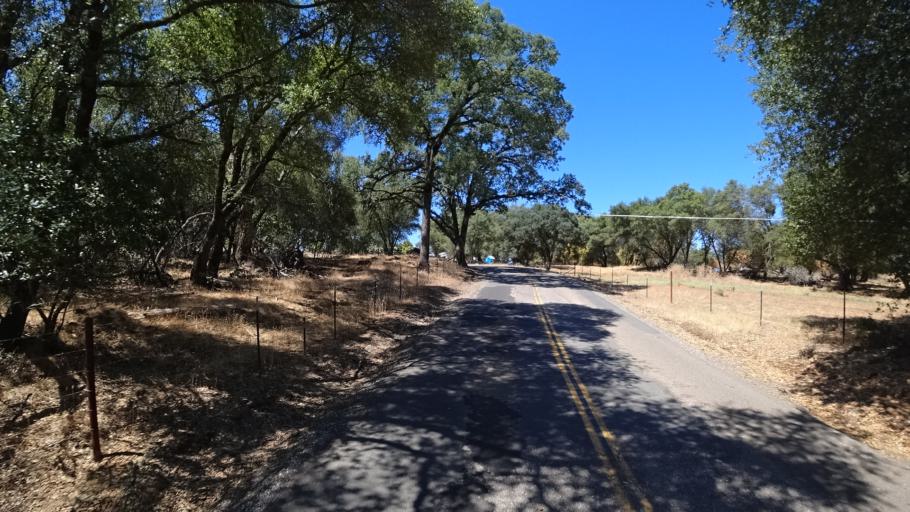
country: US
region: California
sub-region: Calaveras County
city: San Andreas
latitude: 38.1948
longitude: -120.6690
